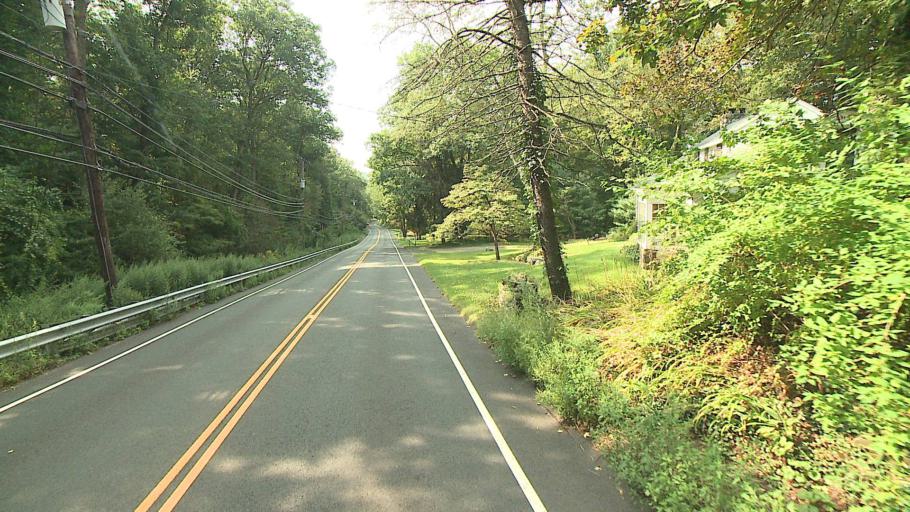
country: US
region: Connecticut
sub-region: Fairfield County
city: Georgetown
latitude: 41.2975
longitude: -73.3890
